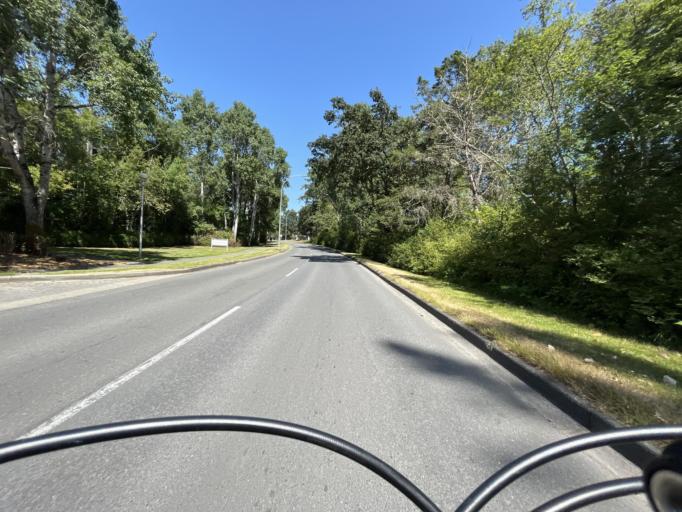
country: CA
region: British Columbia
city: Oak Bay
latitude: 48.4608
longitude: -123.3099
